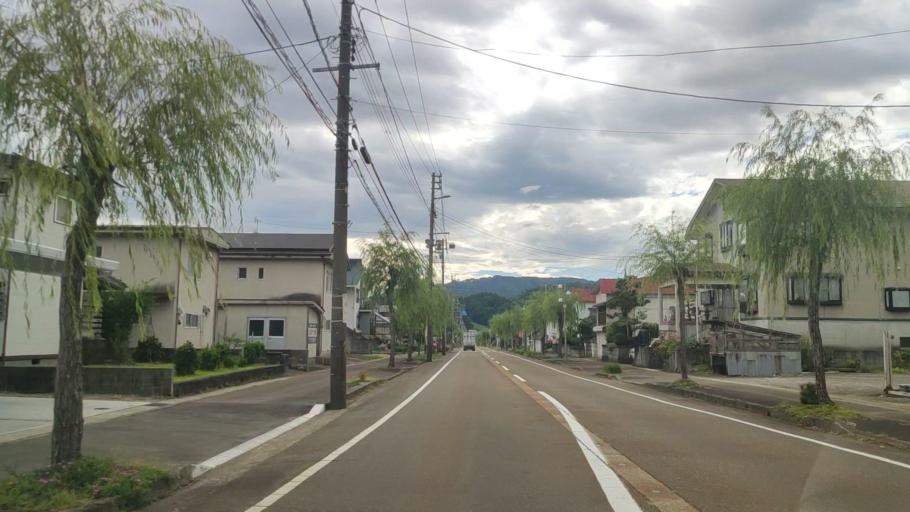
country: JP
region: Niigata
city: Arai
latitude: 37.0190
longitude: 138.2476
